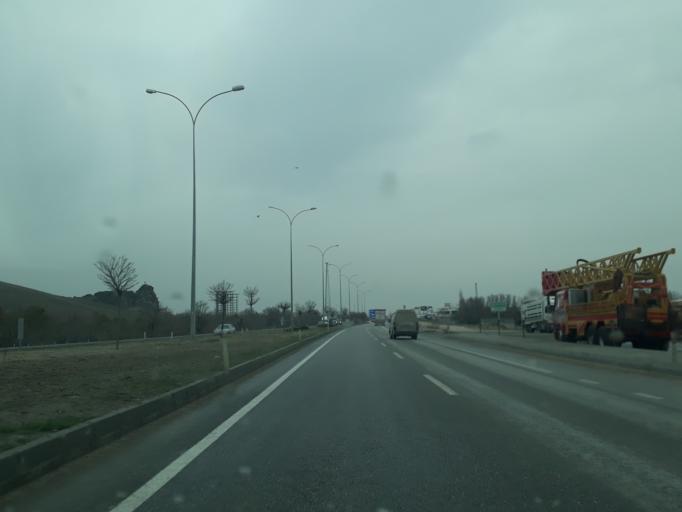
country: TR
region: Konya
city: Karapinar
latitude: 37.7151
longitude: 33.5808
